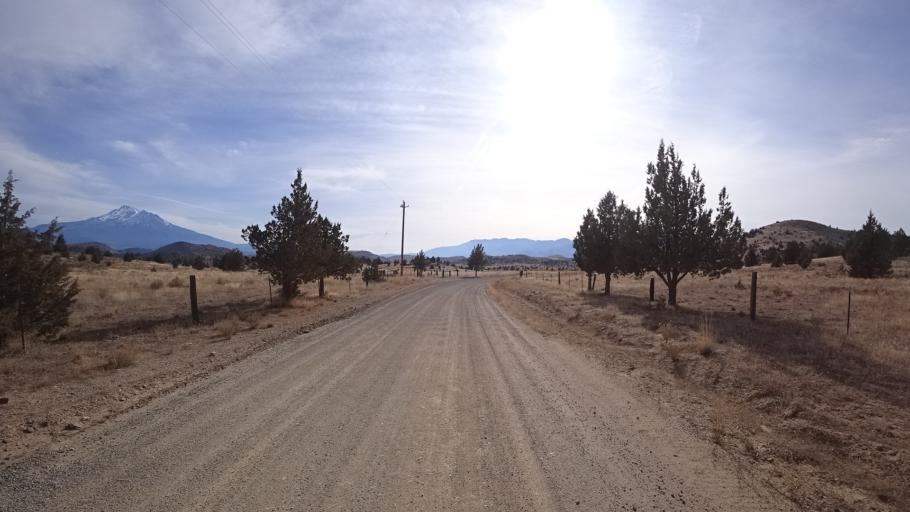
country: US
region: California
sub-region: Siskiyou County
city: Weed
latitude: 41.5639
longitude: -122.4680
